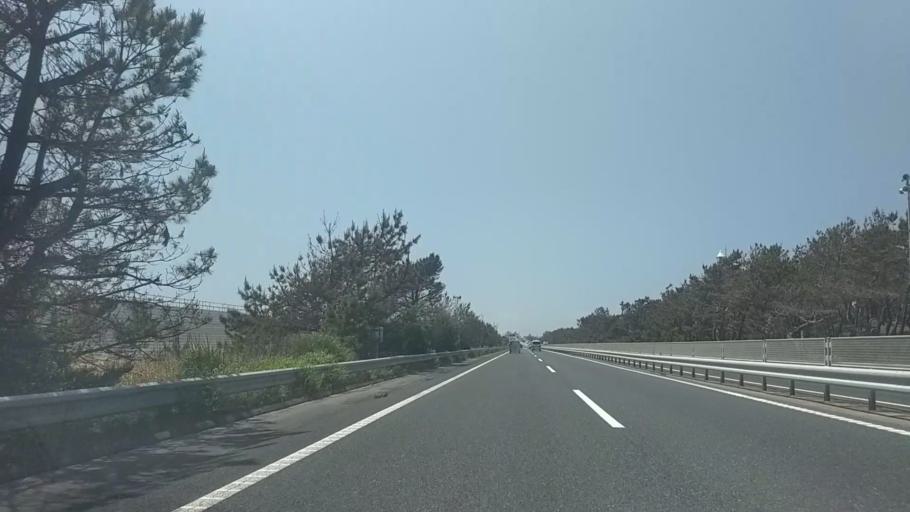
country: JP
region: Shizuoka
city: Kosai-shi
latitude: 34.6780
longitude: 137.6157
